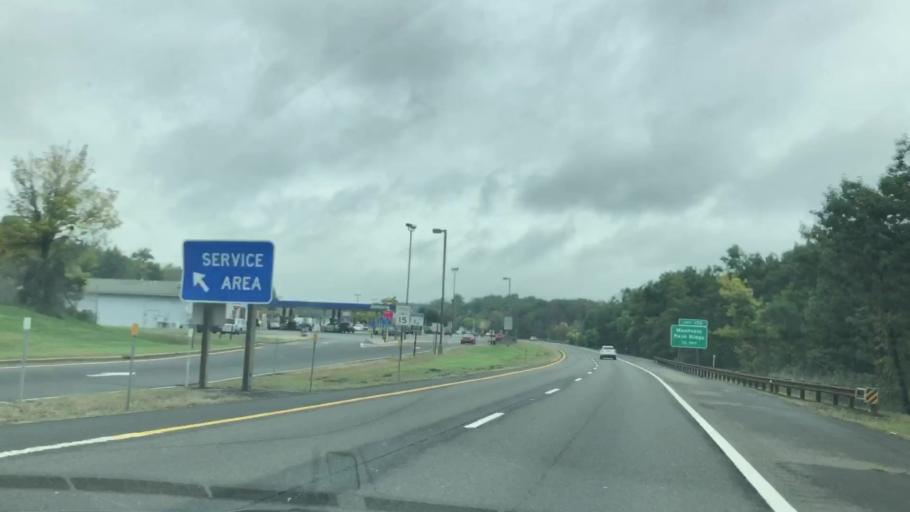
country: US
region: New Jersey
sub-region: Bergen County
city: Woodcliff Lake
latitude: 41.0449
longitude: -74.0673
